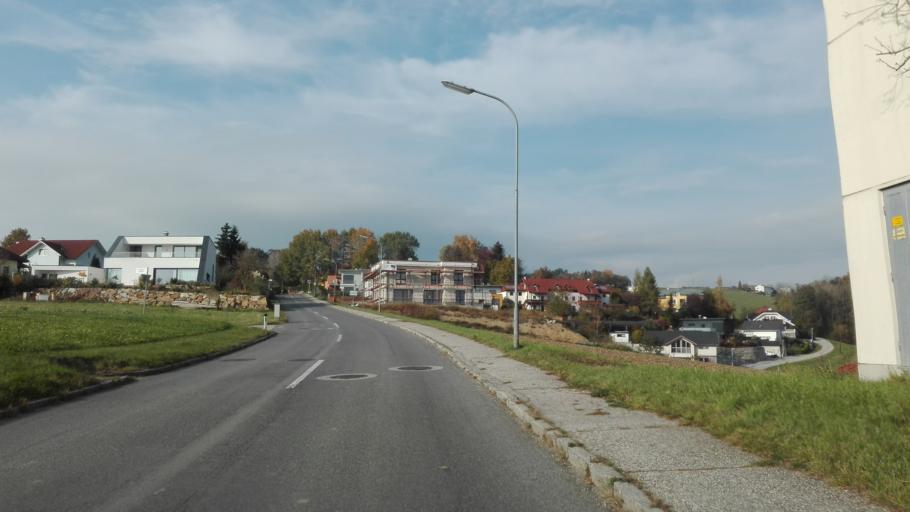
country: AT
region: Upper Austria
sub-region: Politischer Bezirk Perg
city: Perg
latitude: 48.2561
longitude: 14.6261
